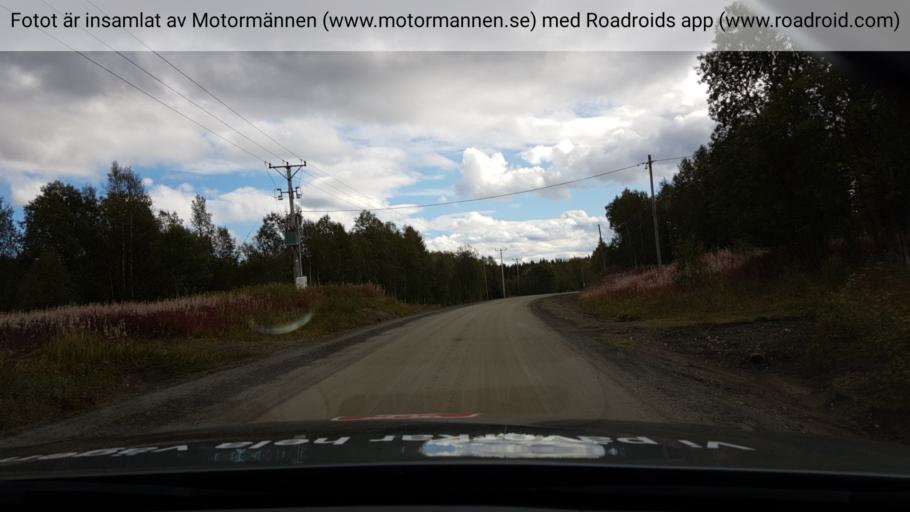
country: SE
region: Jaemtland
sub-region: Are Kommun
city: Are
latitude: 63.7083
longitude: 12.6439
